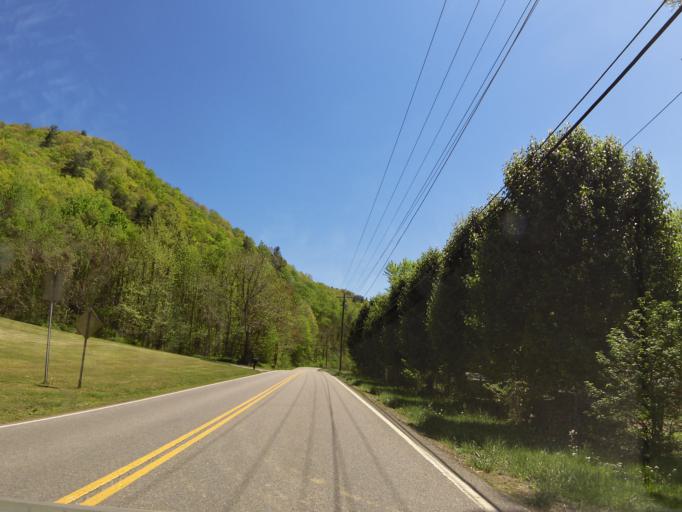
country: US
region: Tennessee
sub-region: Unicoi County
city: Erwin
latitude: 36.1622
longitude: -82.4421
